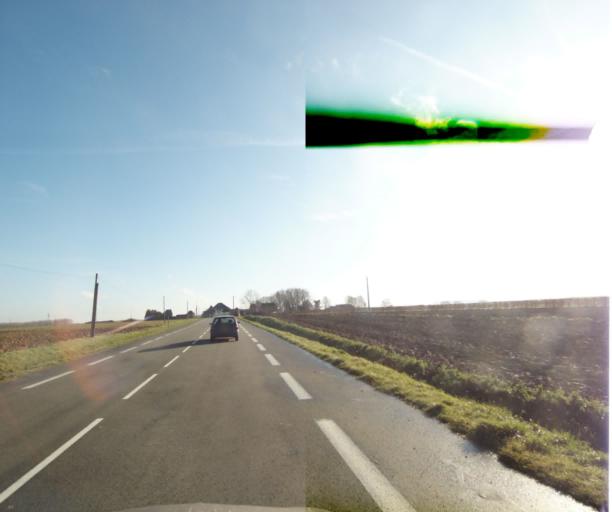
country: FR
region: Nord-Pas-de-Calais
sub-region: Departement du Nord
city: Preseau
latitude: 50.3053
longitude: 3.5852
